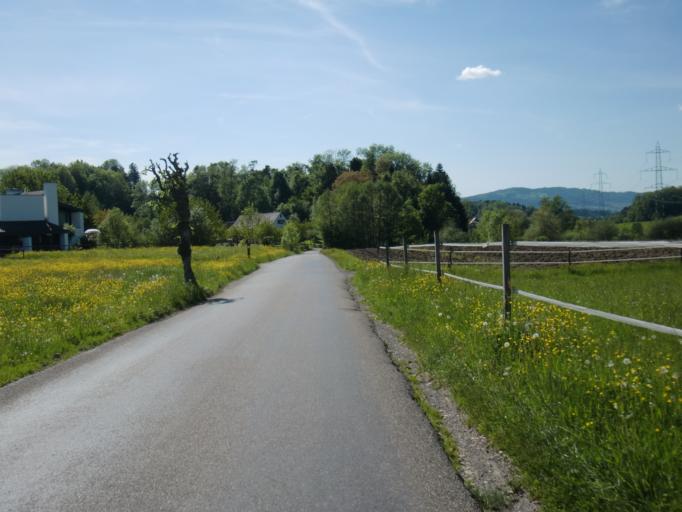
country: CH
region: Zurich
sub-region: Bezirk Hinwil
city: Wolfhausen
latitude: 47.2668
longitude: 8.7856
